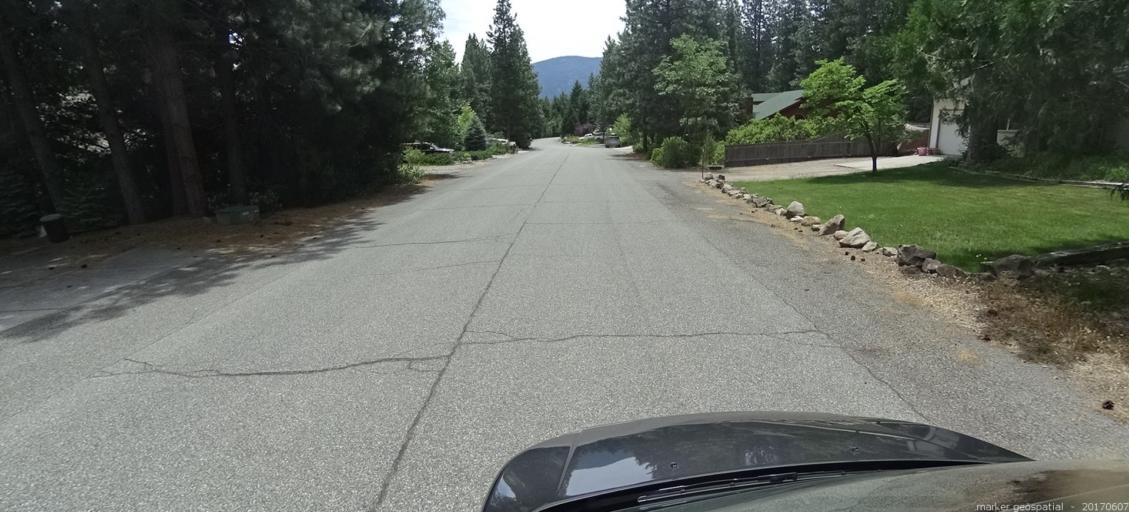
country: US
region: California
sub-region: Siskiyou County
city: Mount Shasta
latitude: 41.2914
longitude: -122.3231
